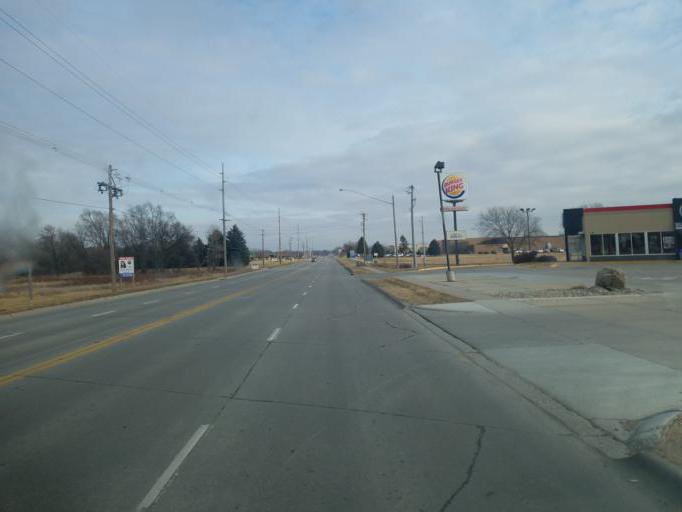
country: US
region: Nebraska
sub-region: Madison County
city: Norfolk
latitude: 42.0472
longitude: -97.4147
